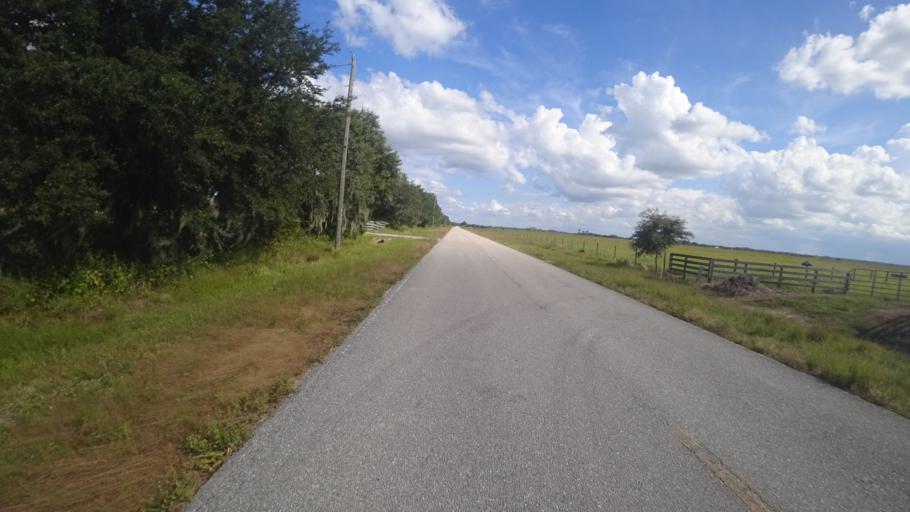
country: US
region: Florida
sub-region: DeSoto County
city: Nocatee
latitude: 27.2713
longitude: -82.1004
